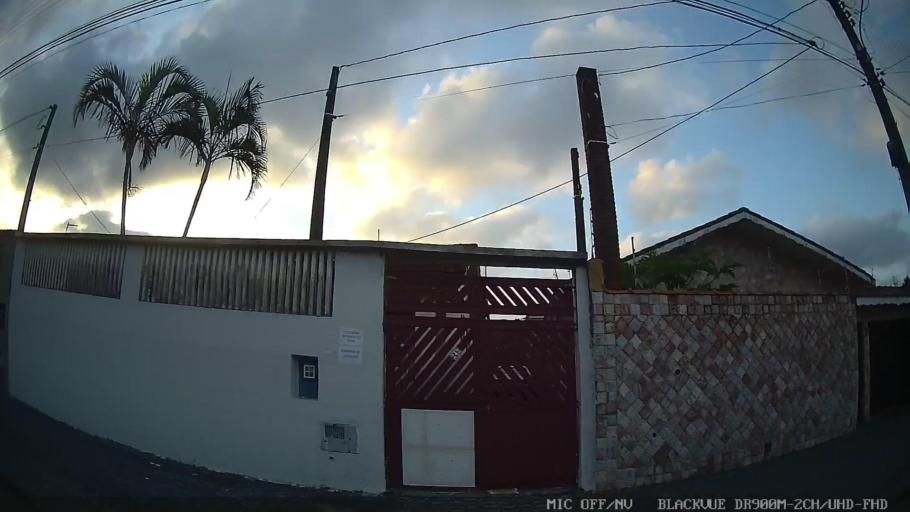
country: BR
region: Sao Paulo
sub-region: Peruibe
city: Peruibe
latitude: -24.3223
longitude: -47.0059
